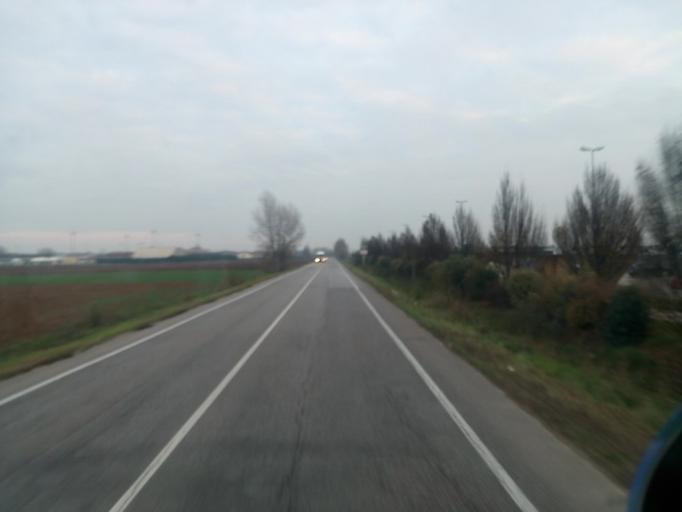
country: IT
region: Veneto
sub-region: Provincia di Verona
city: Pradelle
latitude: 45.2809
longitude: 10.8636
